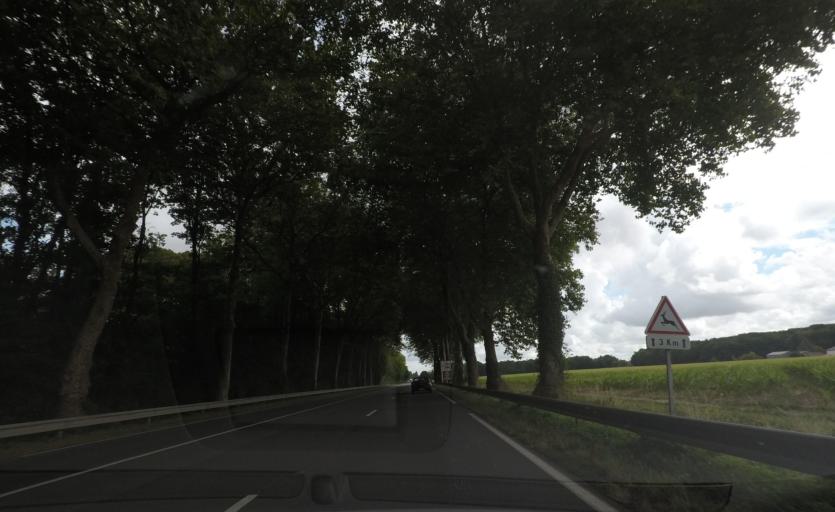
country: FR
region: Pays de la Loire
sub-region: Departement de Maine-et-Loire
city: Pellouailles-les-Vignes
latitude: 47.5279
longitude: -0.4243
